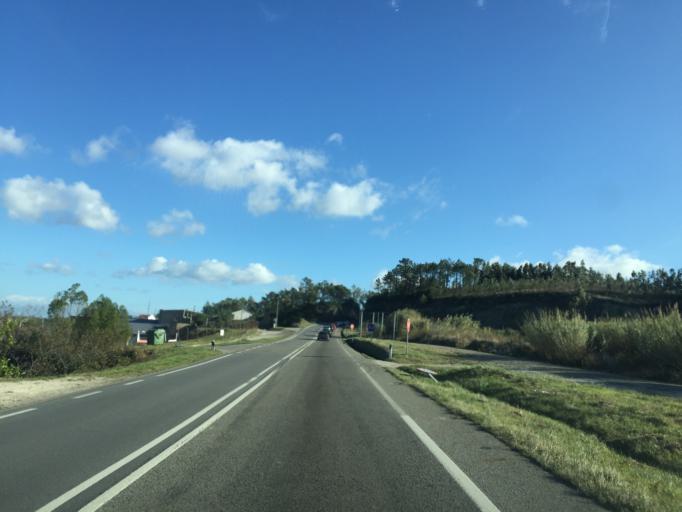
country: PT
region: Coimbra
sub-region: Figueira da Foz
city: Tavarede
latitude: 40.1939
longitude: -8.8326
